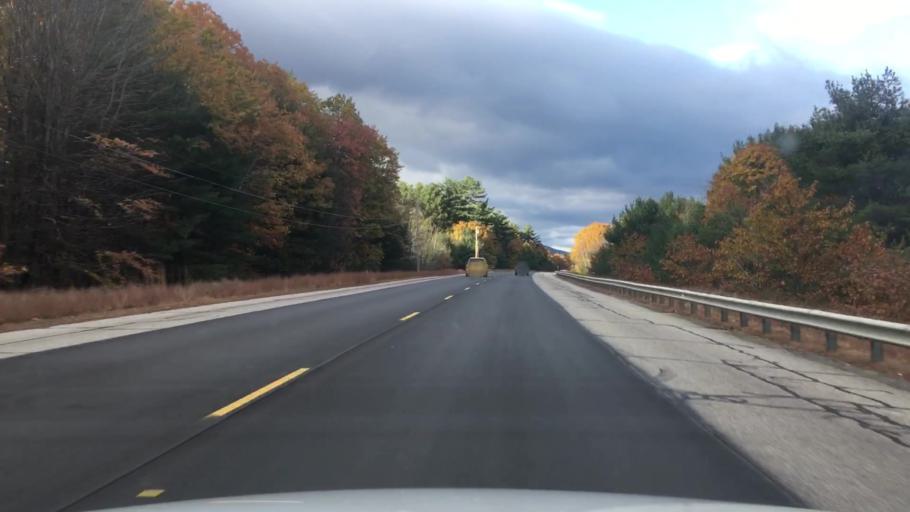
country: US
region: Maine
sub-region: Androscoggin County
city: Livermore
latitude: 44.3489
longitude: -70.2571
